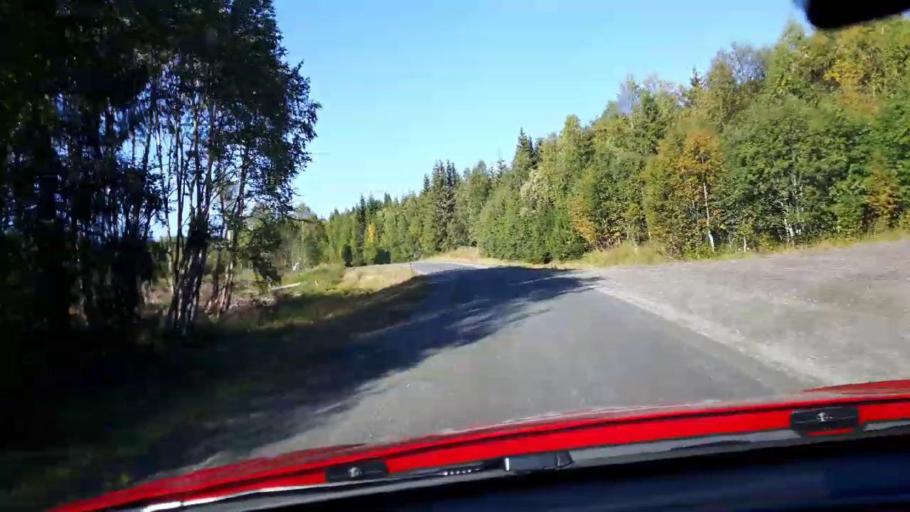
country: NO
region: Nord-Trondelag
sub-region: Lierne
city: Sandvika
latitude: 64.5909
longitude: 13.8544
